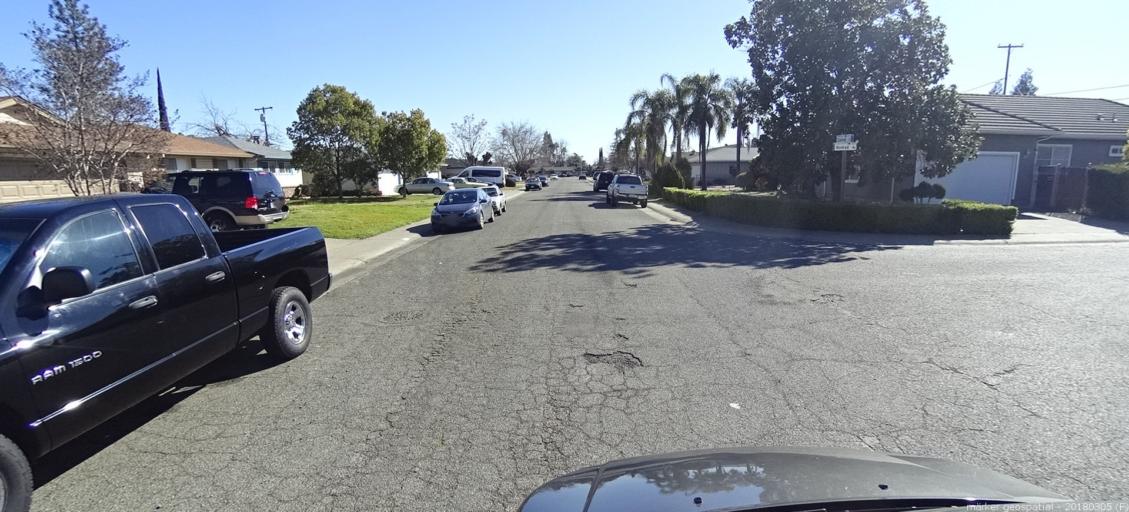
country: US
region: California
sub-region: Sacramento County
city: Florin
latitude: 38.4949
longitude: -121.4188
